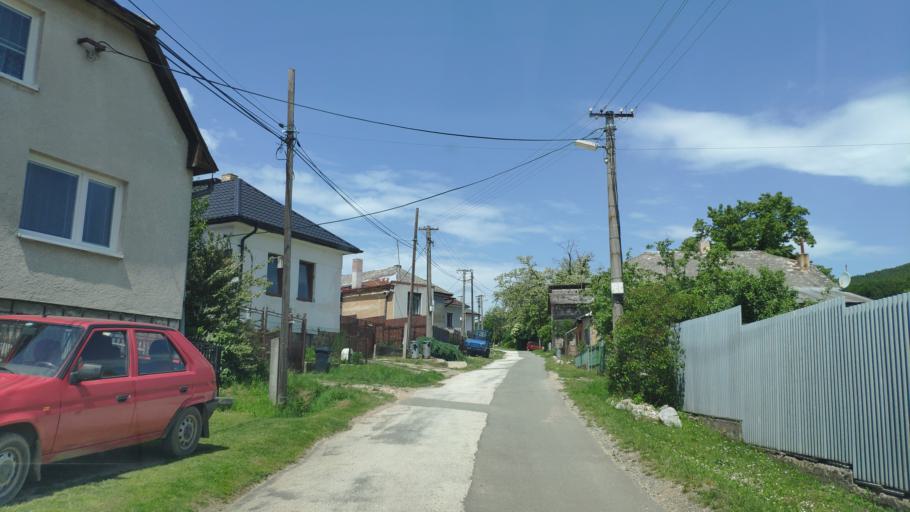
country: SK
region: Kosicky
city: Medzev
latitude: 48.7157
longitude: 20.9731
